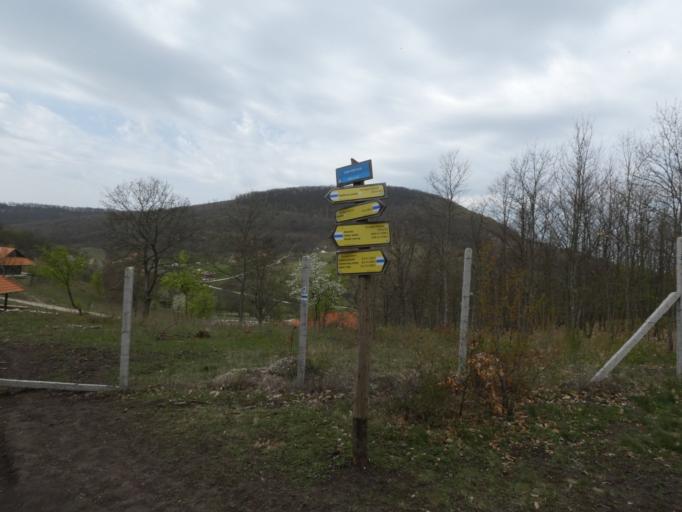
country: HU
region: Nograd
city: Rimoc
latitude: 47.9811
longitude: 19.6031
